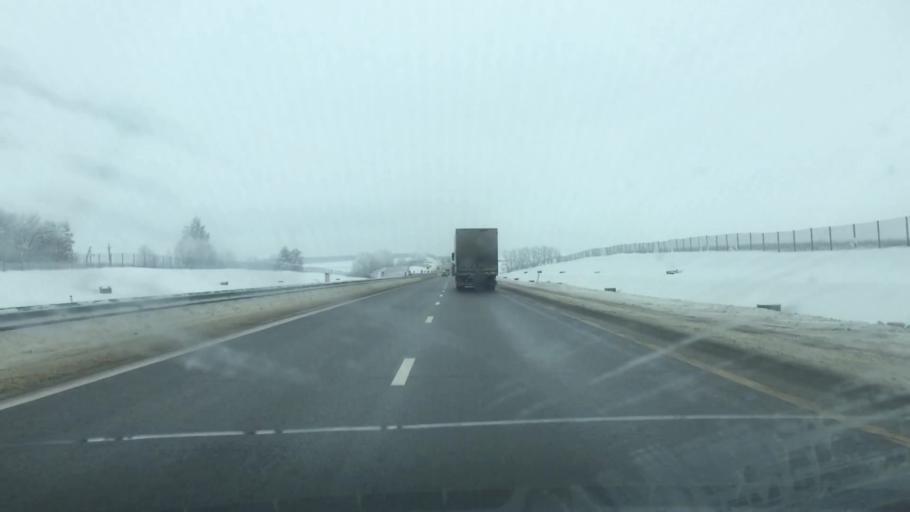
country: RU
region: Tula
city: Kazachka
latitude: 53.3354
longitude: 38.1806
